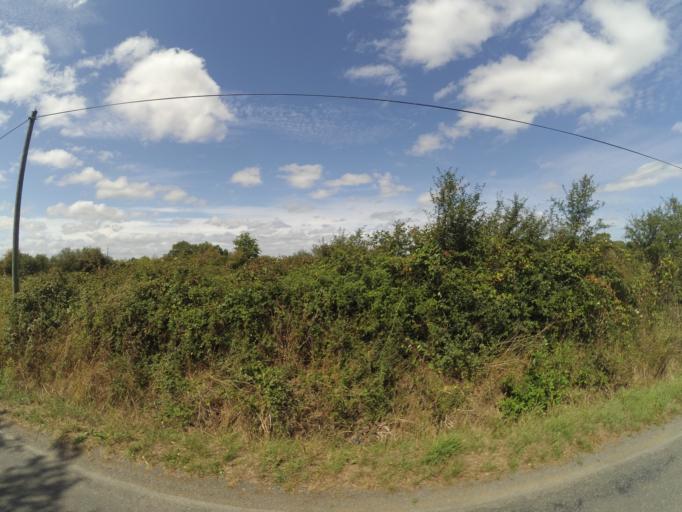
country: FR
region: Pays de la Loire
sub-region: Departement de la Loire-Atlantique
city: Saint-Hilaire-de-Clisson
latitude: 47.0787
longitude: -1.3019
